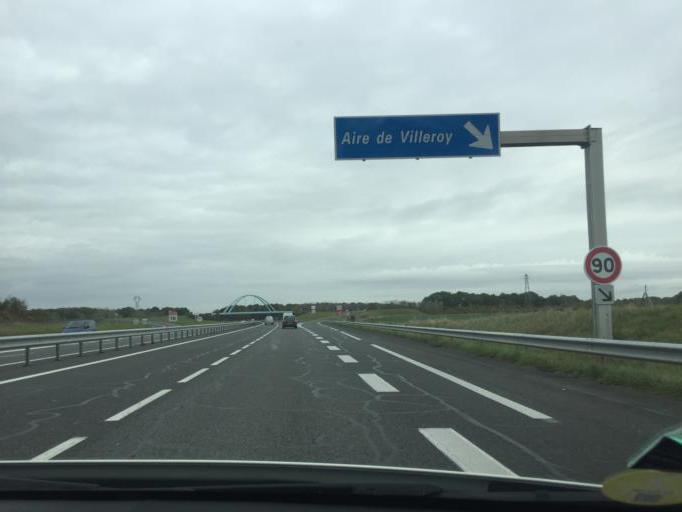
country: FR
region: Bourgogne
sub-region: Departement de l'Yonne
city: Egriselles-le-Bocage
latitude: 48.1622
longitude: 3.1755
